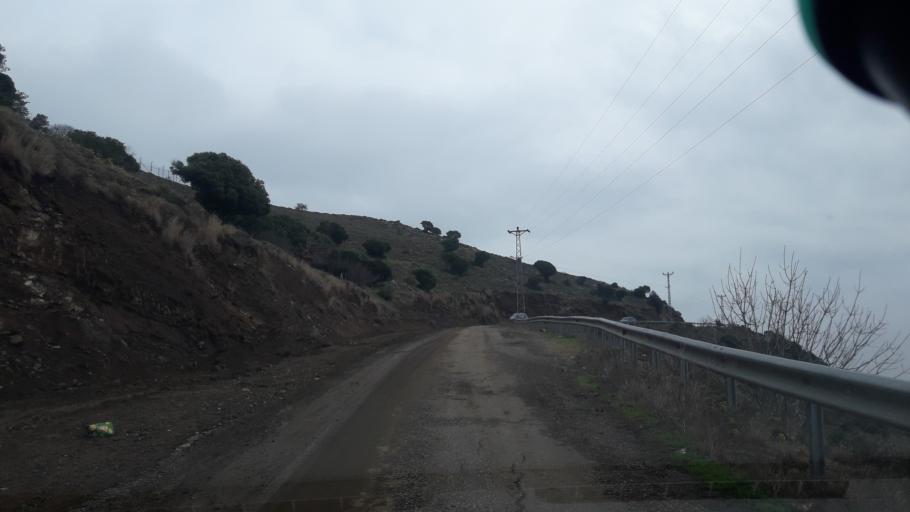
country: TR
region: Sinop
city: Sinop
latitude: 42.0175
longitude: 35.2000
